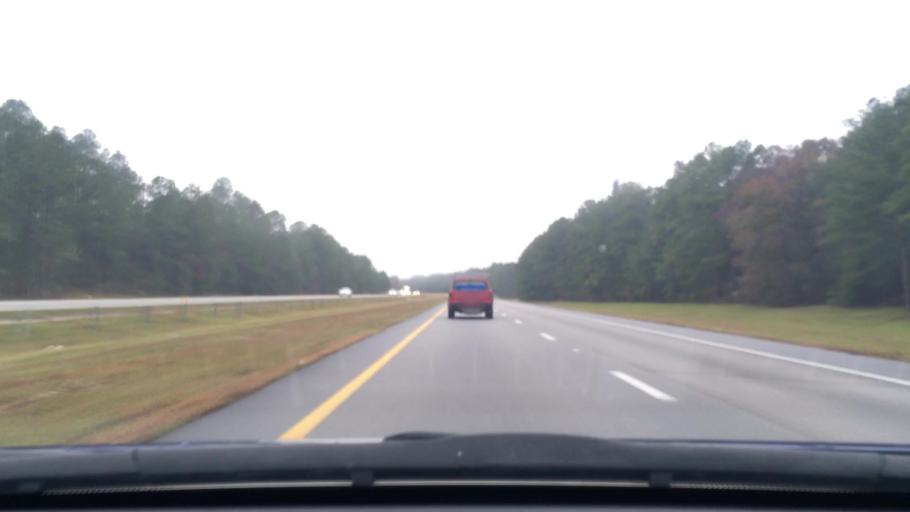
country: US
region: South Carolina
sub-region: Lee County
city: Bishopville
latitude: 34.1980
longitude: -80.3404
